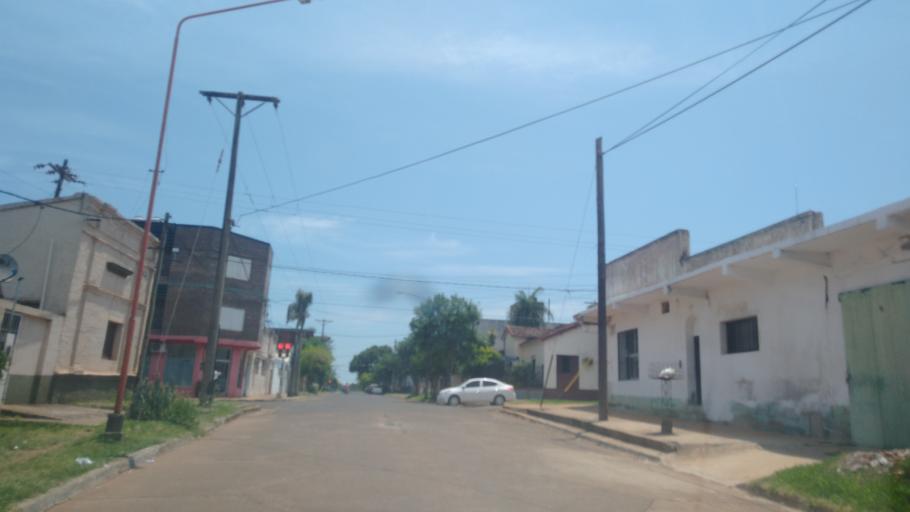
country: AR
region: Corrientes
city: Santo Tome
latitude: -28.5511
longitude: -56.0380
